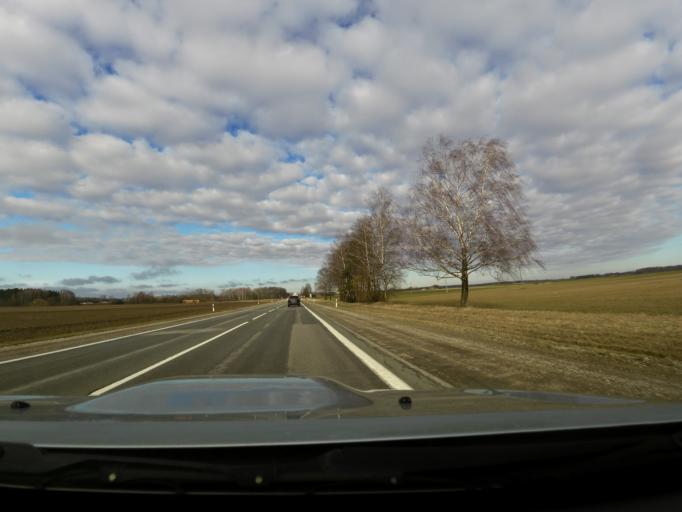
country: LT
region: Panevezys
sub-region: Panevezys City
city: Panevezys
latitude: 55.7510
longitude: 24.1398
